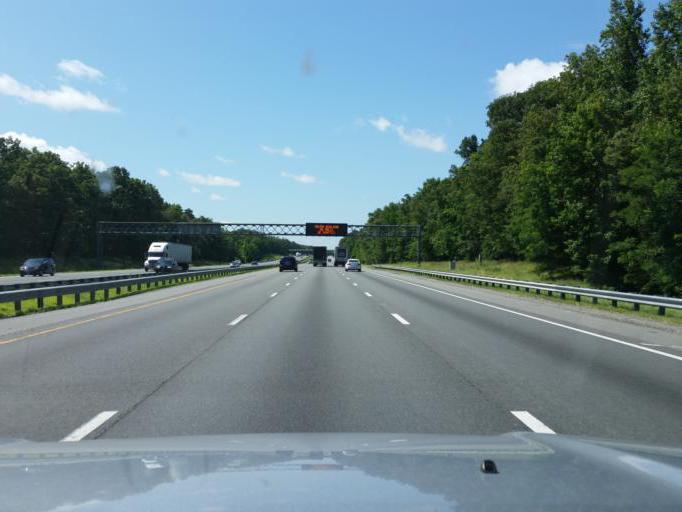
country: US
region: Virginia
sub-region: Spotsylvania County
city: Spotsylvania Courthouse
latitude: 38.1871
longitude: -77.5013
